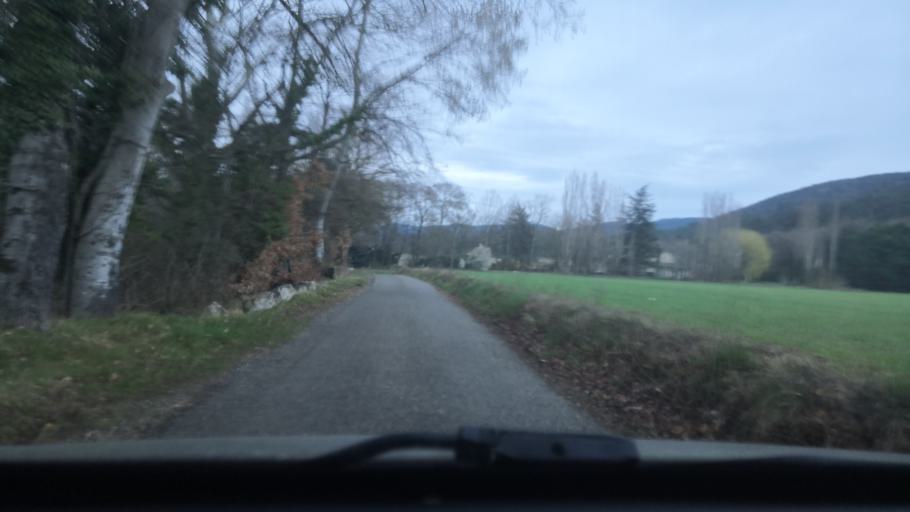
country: FR
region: Rhone-Alpes
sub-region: Departement de la Drome
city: Dieulefit
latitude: 44.5293
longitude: 5.0061
